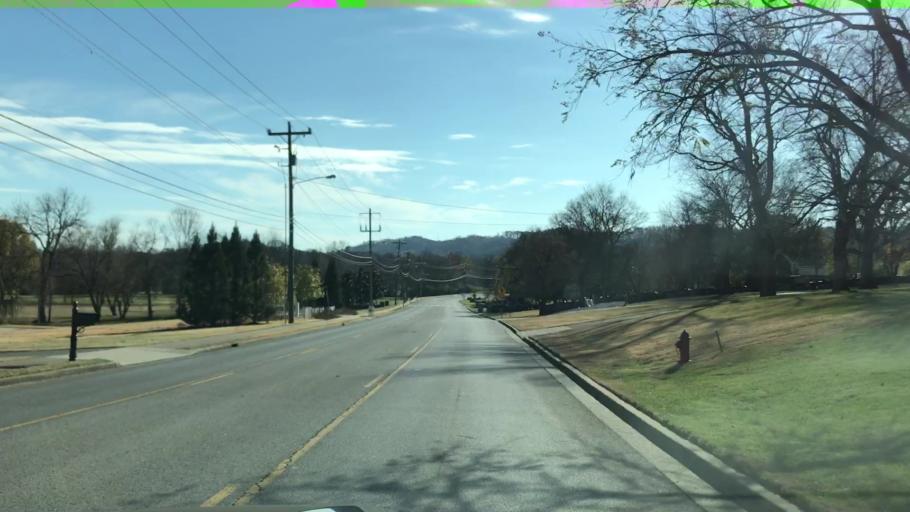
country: US
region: Tennessee
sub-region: Williamson County
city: Brentwood
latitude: 36.0285
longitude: -86.8182
